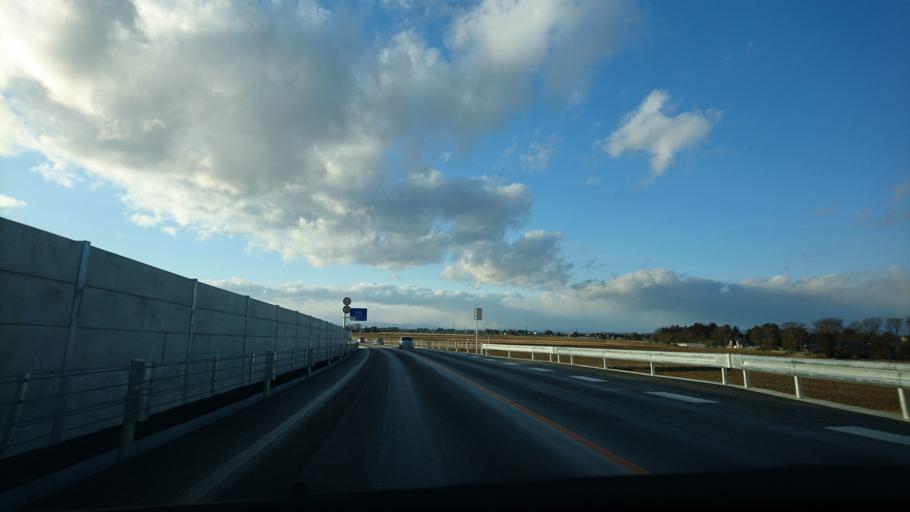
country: JP
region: Miyagi
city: Wakuya
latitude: 38.6843
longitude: 141.2489
